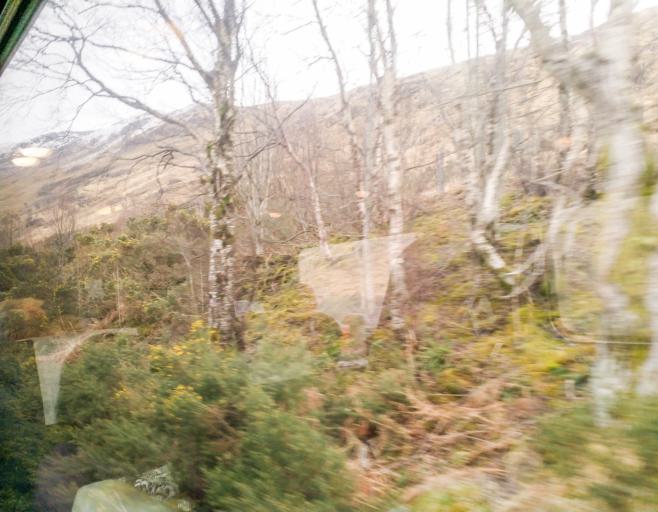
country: GB
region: Scotland
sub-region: Highland
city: Spean Bridge
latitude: 56.8168
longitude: -4.7145
